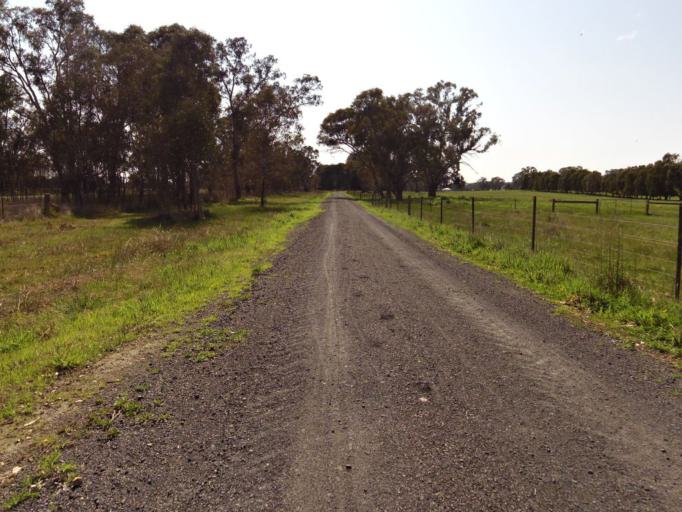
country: AU
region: Victoria
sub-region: Murrindindi
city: Alexandra
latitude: -37.1136
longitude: 145.6080
